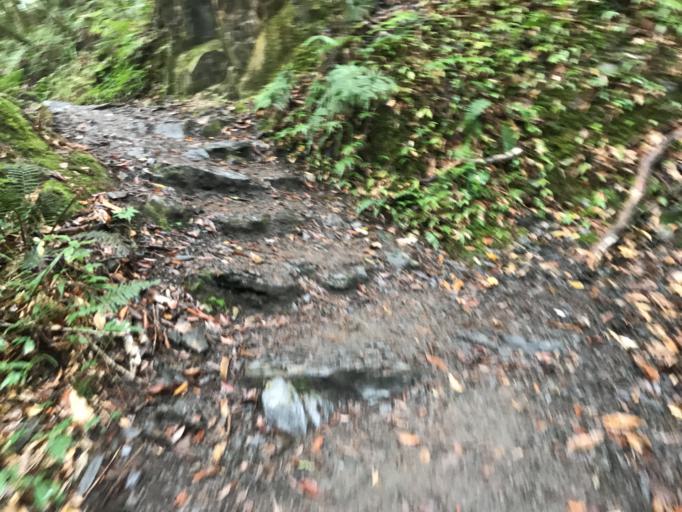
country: TW
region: Taiwan
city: Daxi
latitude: 24.5477
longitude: 121.2920
